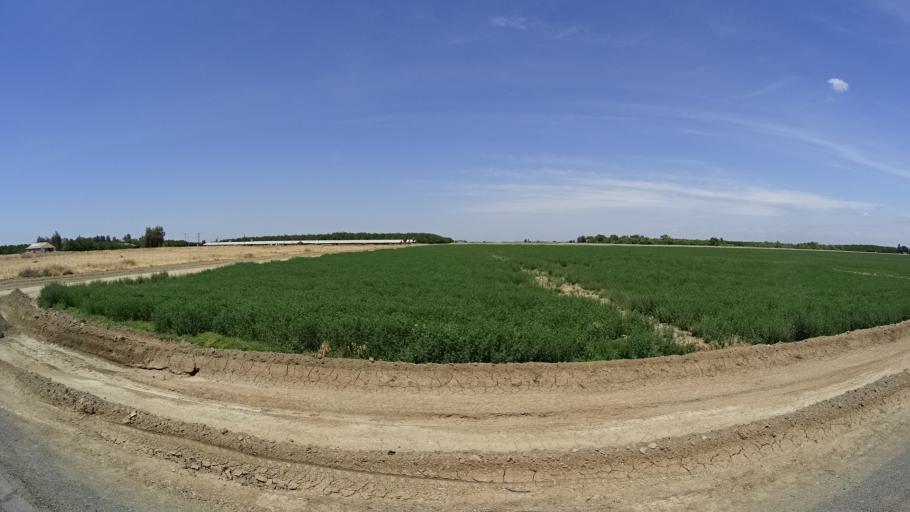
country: US
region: California
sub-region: Kings County
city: Armona
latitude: 36.2838
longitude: -119.6813
